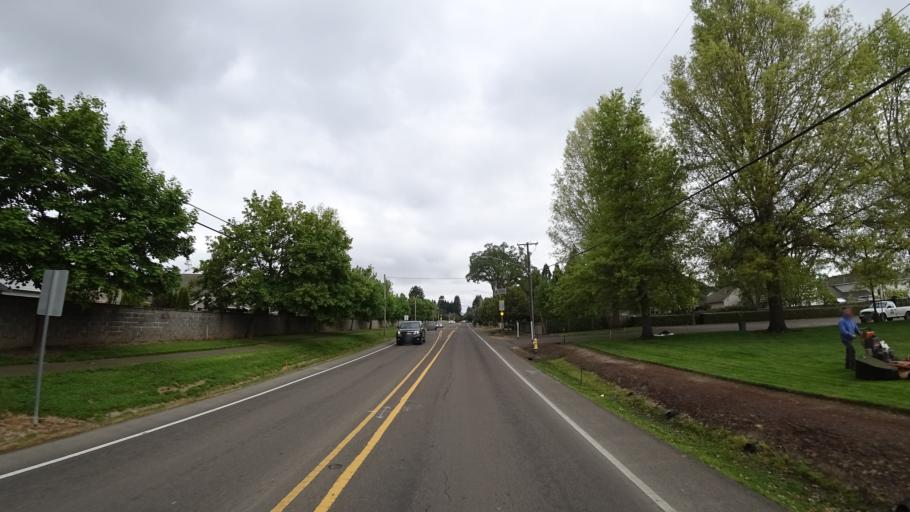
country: US
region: Oregon
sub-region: Washington County
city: Hillsboro
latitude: 45.5410
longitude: -122.9797
